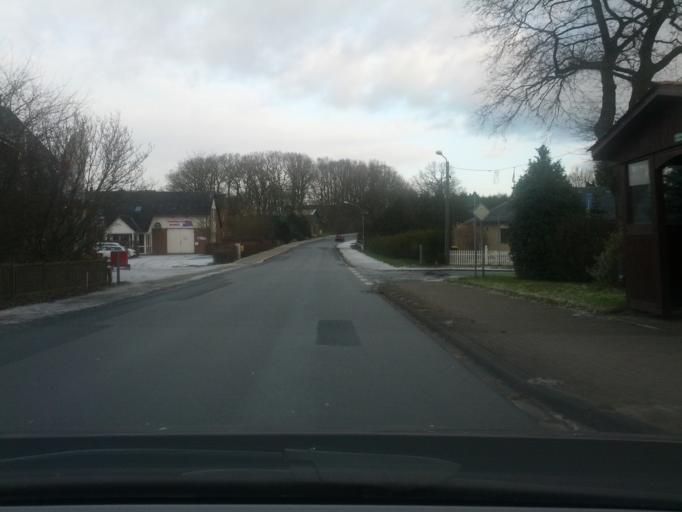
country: DE
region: Lower Saxony
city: Beckdorf
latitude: 53.4092
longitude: 9.6102
